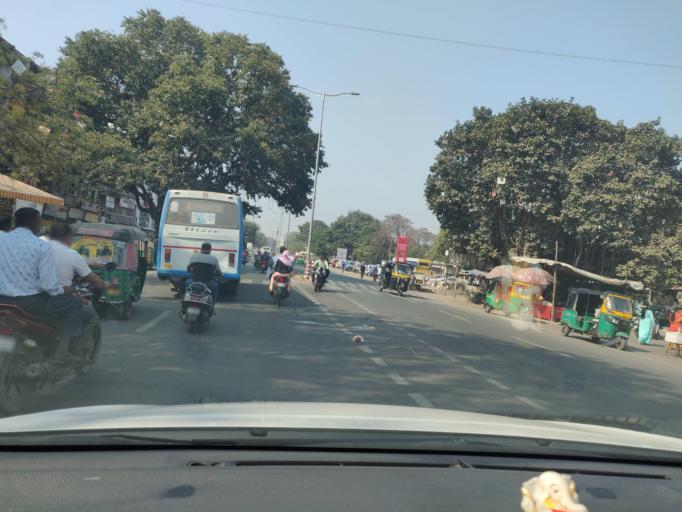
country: IN
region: Gujarat
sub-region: Vadodara
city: Vadodara
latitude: 22.3009
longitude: 73.2236
